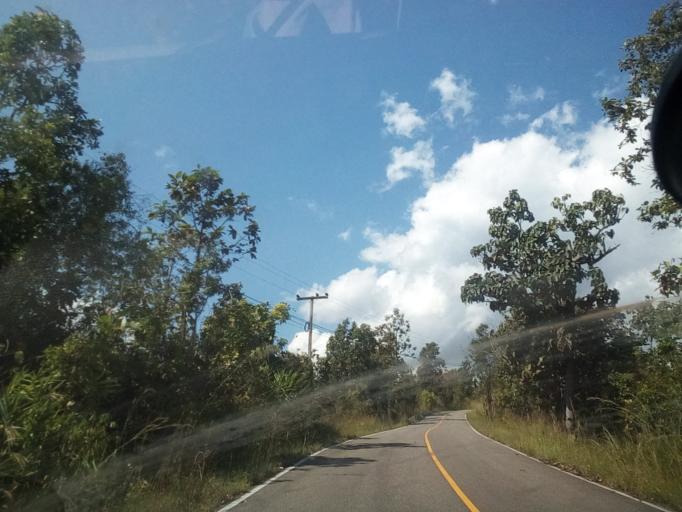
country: TH
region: Chiang Mai
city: Samoeng
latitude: 18.8691
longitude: 98.6924
